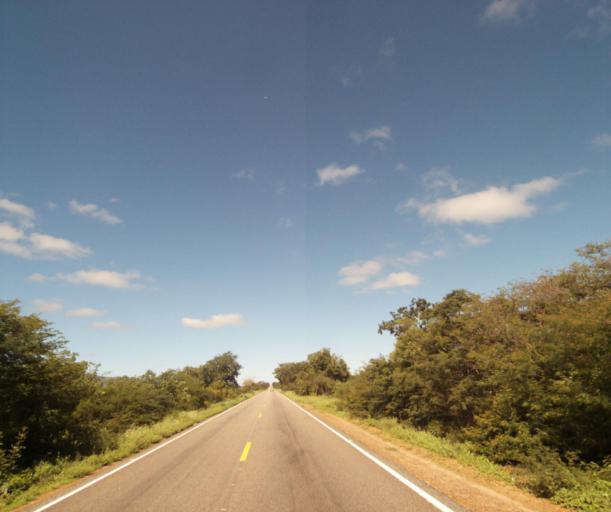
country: BR
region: Bahia
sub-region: Palmas De Monte Alto
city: Palmas de Monte Alto
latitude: -14.2422
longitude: -43.0712
